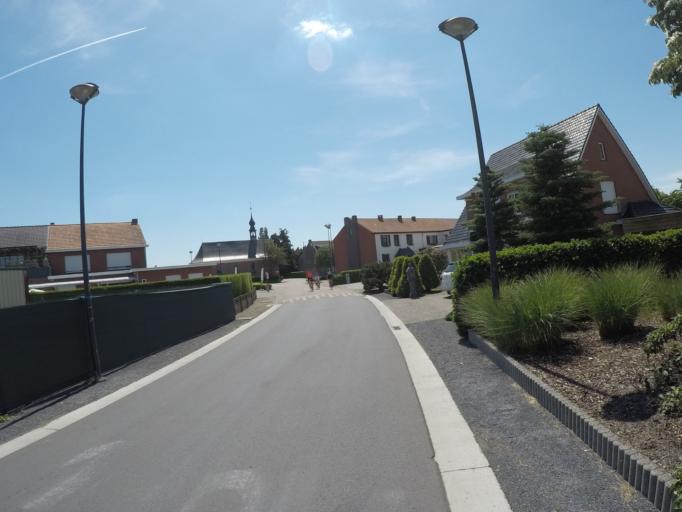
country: BE
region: Flanders
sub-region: Provincie Antwerpen
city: Wuustwezel
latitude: 51.3802
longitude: 4.5607
